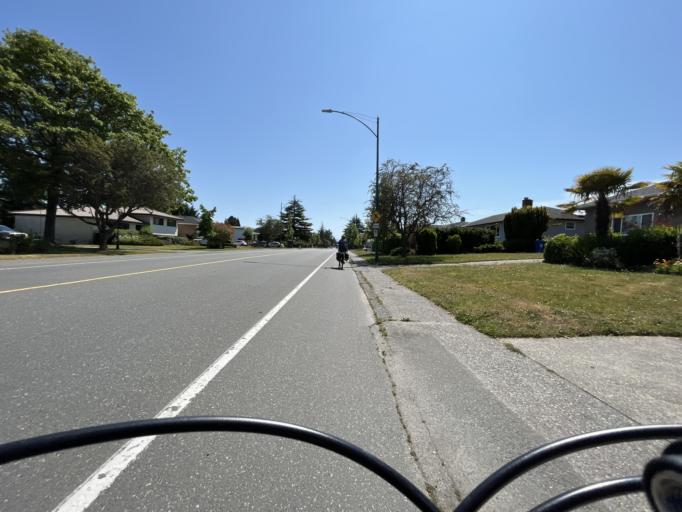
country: CA
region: British Columbia
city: Oak Bay
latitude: 48.4542
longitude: -123.3147
